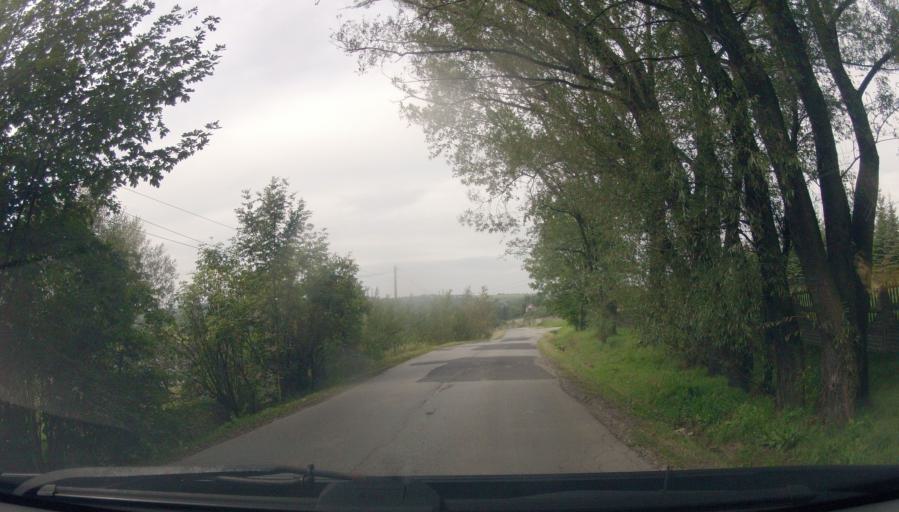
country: PL
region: Lesser Poland Voivodeship
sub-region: Powiat krakowski
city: Ochojno
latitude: 49.9435
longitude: 19.9976
